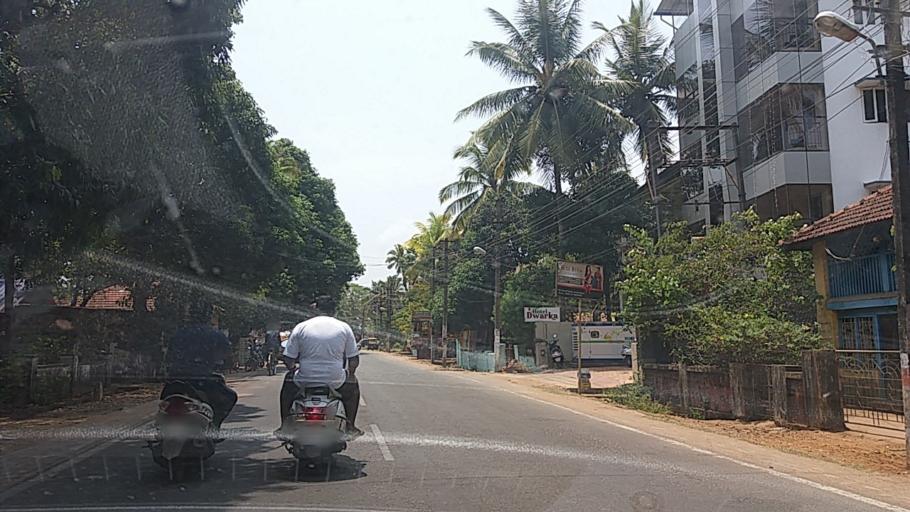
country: IN
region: Karnataka
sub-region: Uttar Kannada
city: Karwar
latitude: 14.8108
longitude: 74.1401
